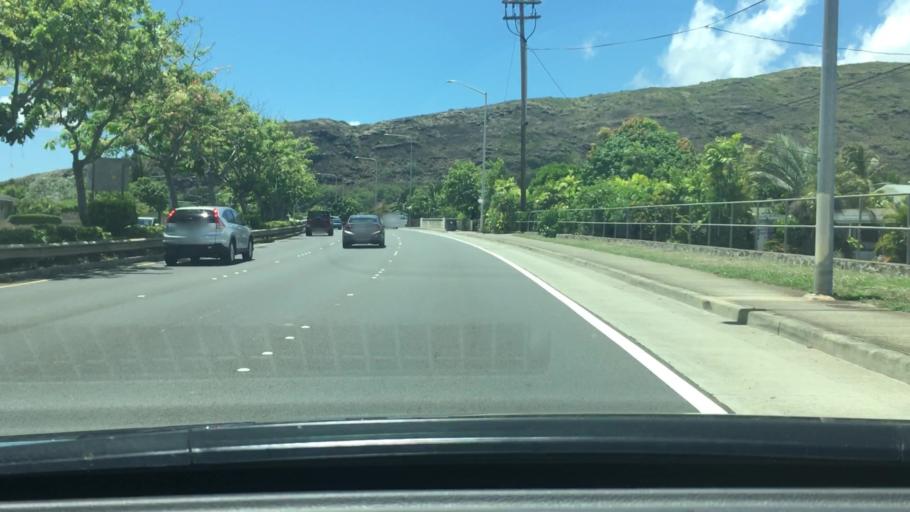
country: US
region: Hawaii
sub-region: Honolulu County
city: Waimanalo Beach
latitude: 21.2863
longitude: -157.7207
